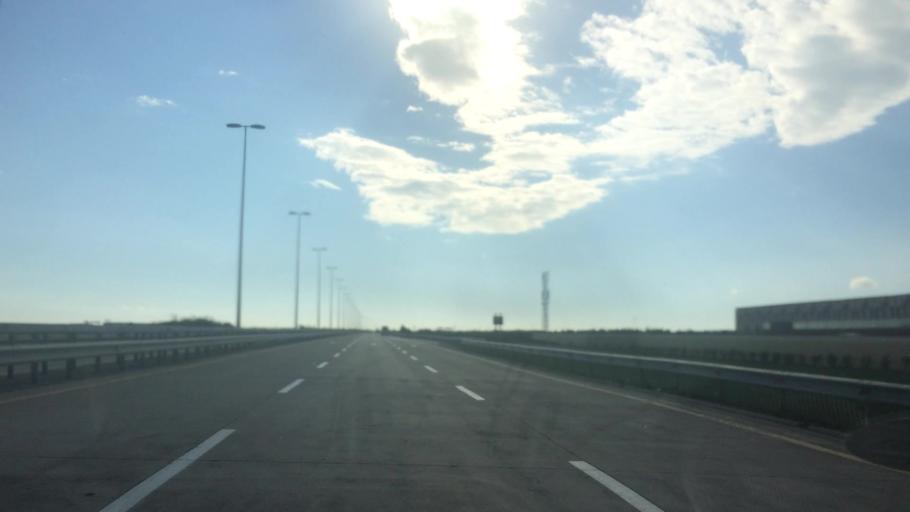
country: AZ
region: Baki
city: Hovsan
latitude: 40.3859
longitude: 50.0652
